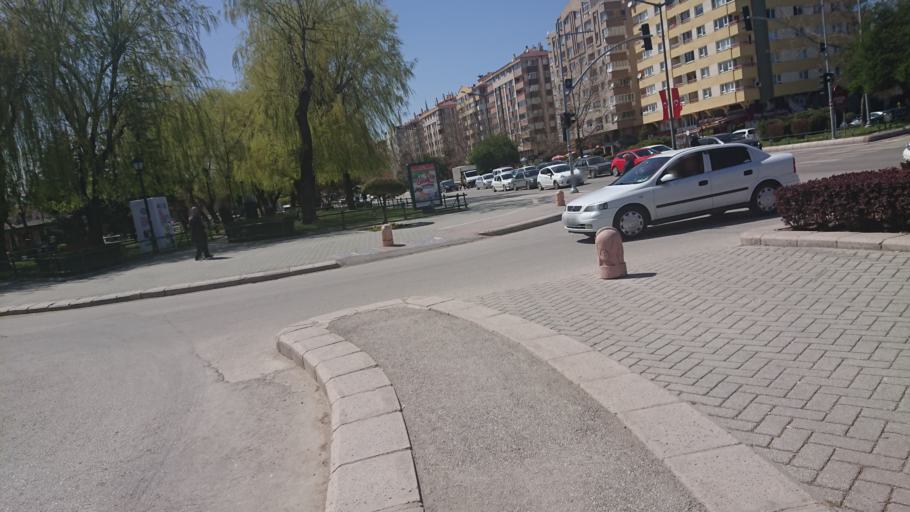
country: TR
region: Eskisehir
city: Eskisehir
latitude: 39.7647
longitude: 30.5094
